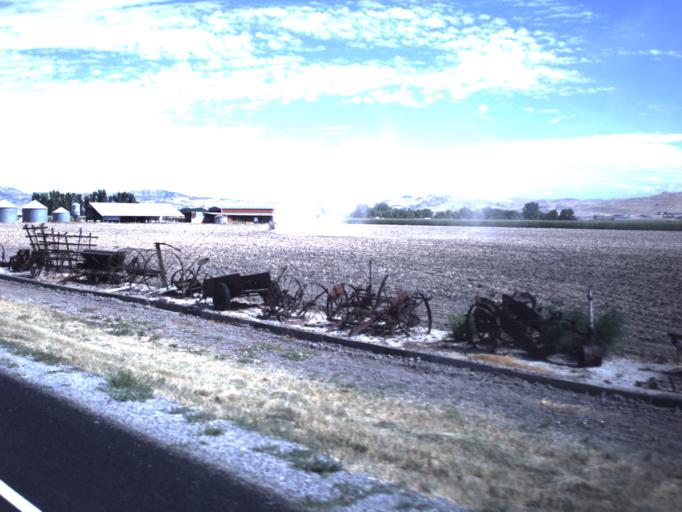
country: US
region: Utah
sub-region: Box Elder County
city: Garland
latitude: 41.7346
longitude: -112.1433
